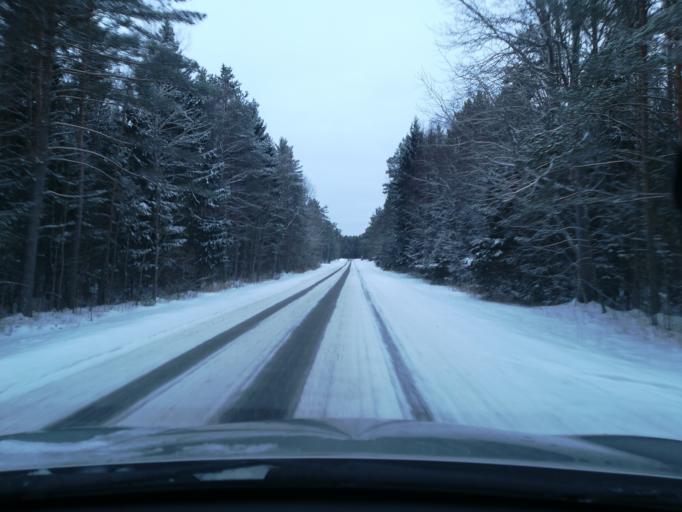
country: EE
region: Harju
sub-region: Keila linn
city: Keila
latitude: 59.3890
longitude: 24.2959
